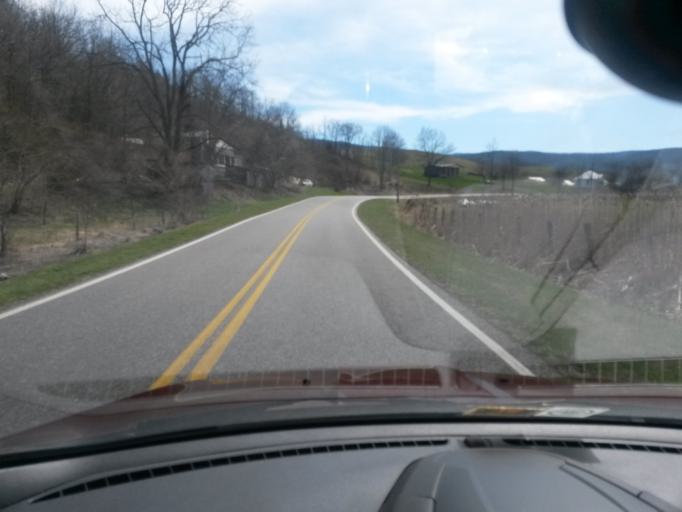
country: US
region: West Virginia
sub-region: Greenbrier County
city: White Sulphur Springs
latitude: 37.6538
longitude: -80.2359
